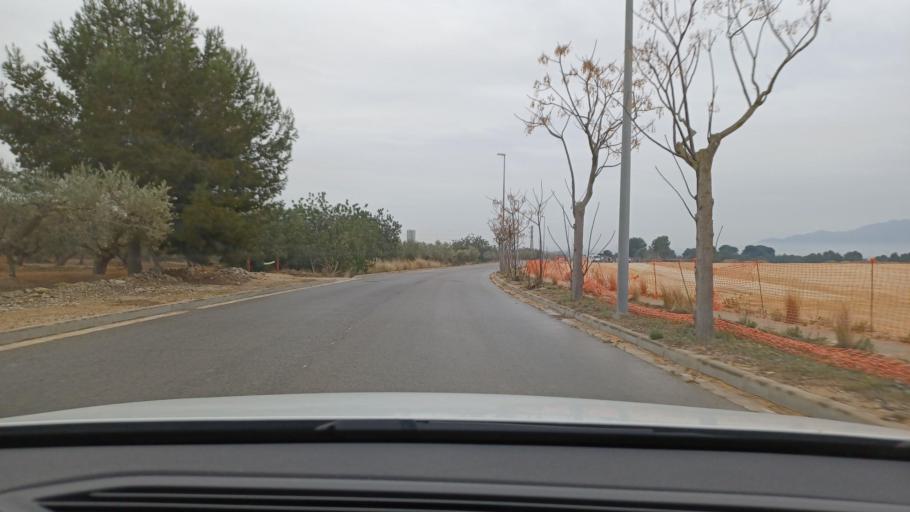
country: ES
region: Catalonia
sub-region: Provincia de Tarragona
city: Amposta
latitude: 40.7659
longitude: 0.5985
